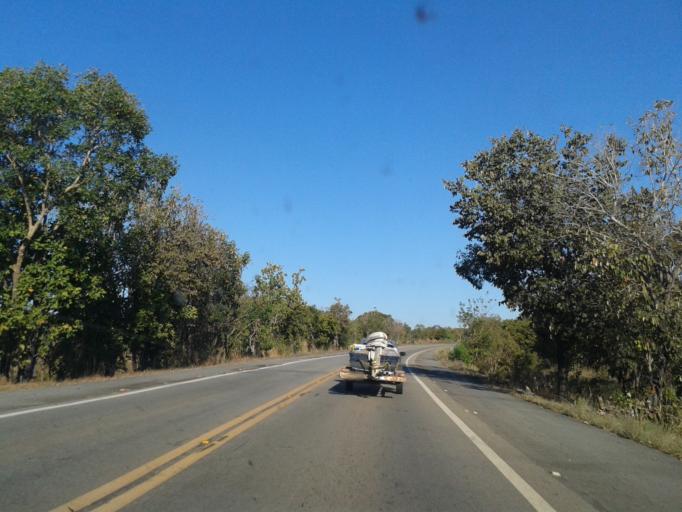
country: BR
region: Goias
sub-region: Itapuranga
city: Itapuranga
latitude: -15.3613
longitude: -50.3944
